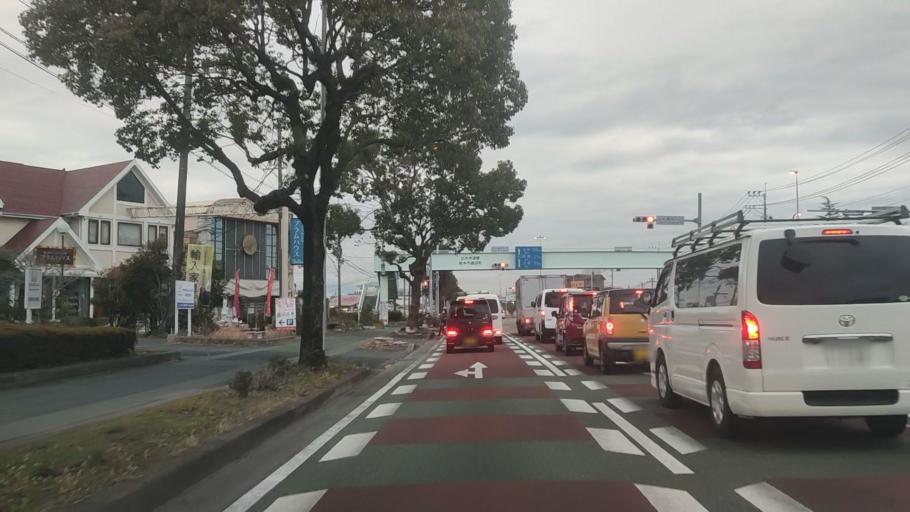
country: JP
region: Kumamoto
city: Kumamoto
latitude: 32.7707
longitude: 130.7296
